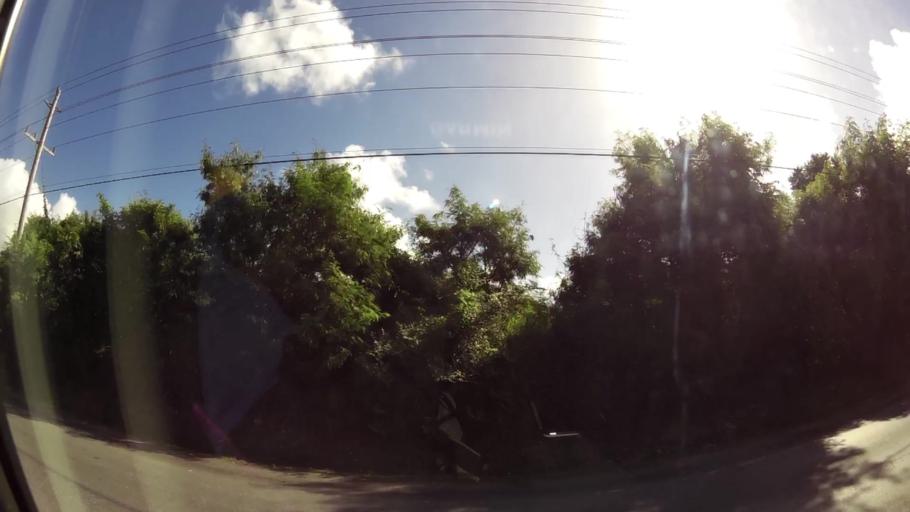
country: BB
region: Saint James
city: Holetown
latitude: 13.2082
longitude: -59.6175
